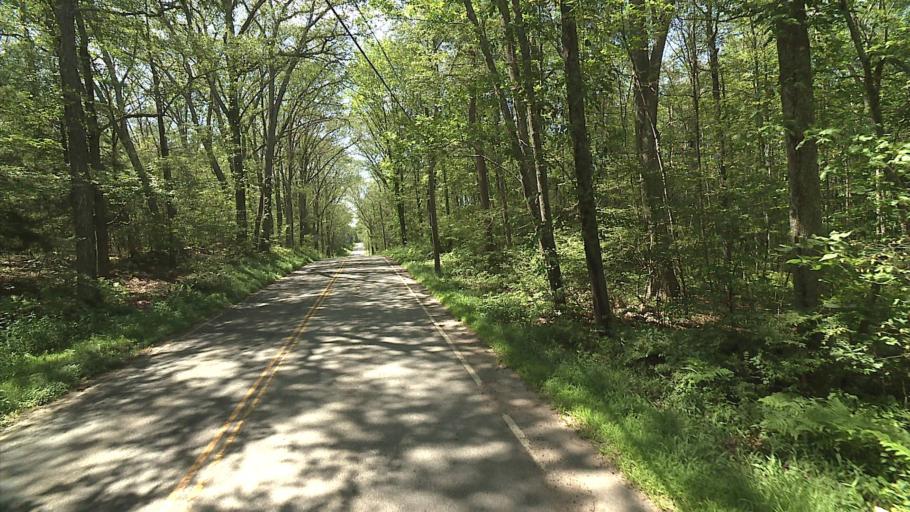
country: US
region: Connecticut
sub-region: Windham County
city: South Woodstock
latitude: 41.8747
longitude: -71.9860
